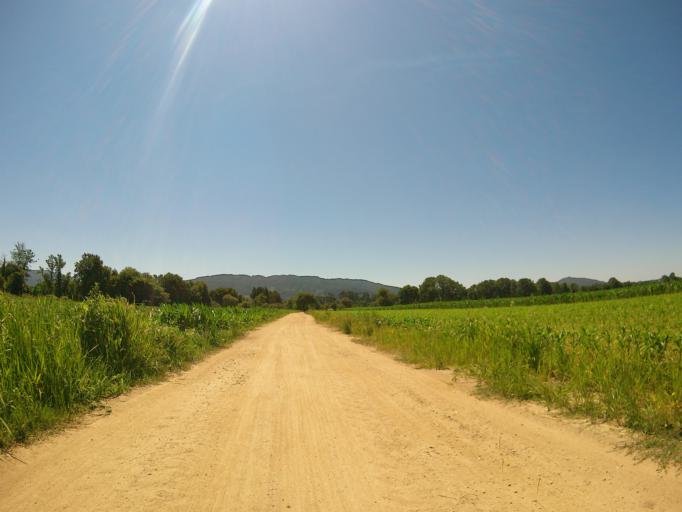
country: PT
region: Viana do Castelo
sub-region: Viana do Castelo
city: Darque
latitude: 41.7198
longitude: -8.7051
